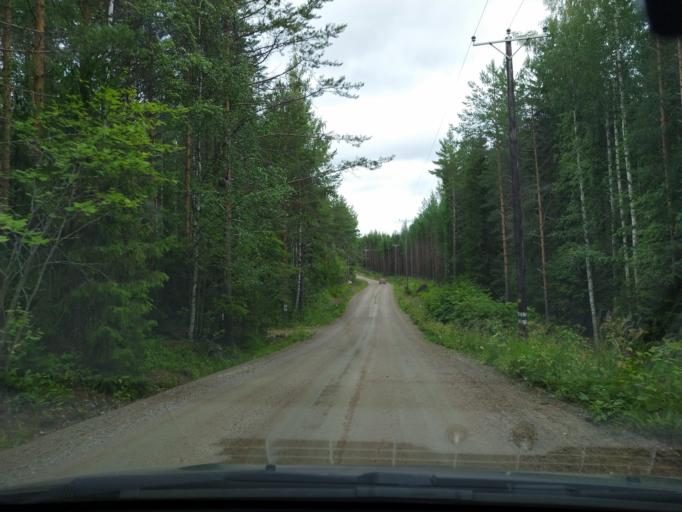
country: FI
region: Southern Savonia
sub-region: Mikkeli
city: Maentyharju
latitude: 61.1400
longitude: 26.8886
